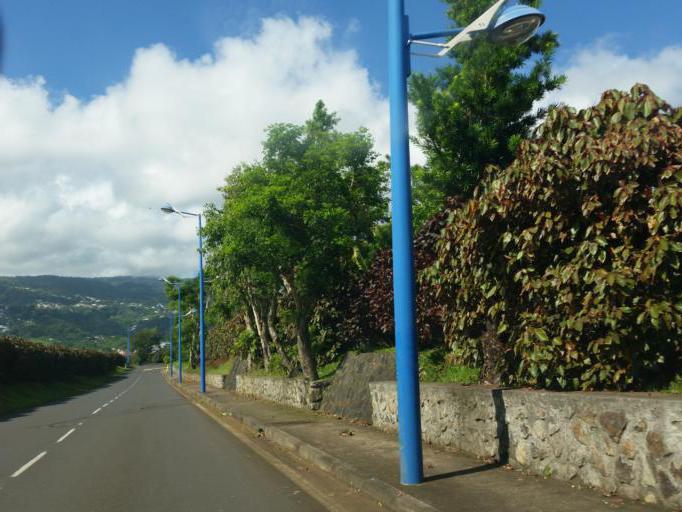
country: RE
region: Reunion
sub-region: Reunion
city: Sainte-Marie
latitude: -20.9233
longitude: 55.5309
